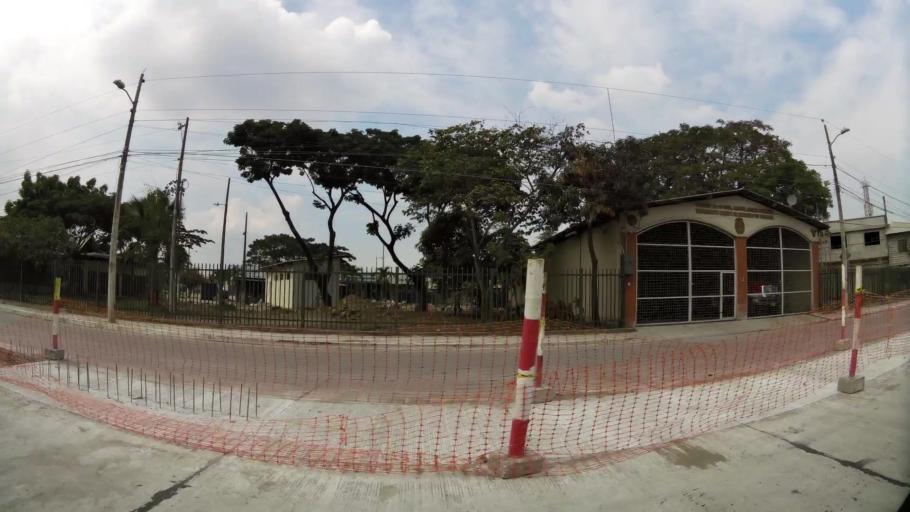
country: EC
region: Guayas
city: Guayaquil
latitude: -2.2490
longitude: -79.9250
